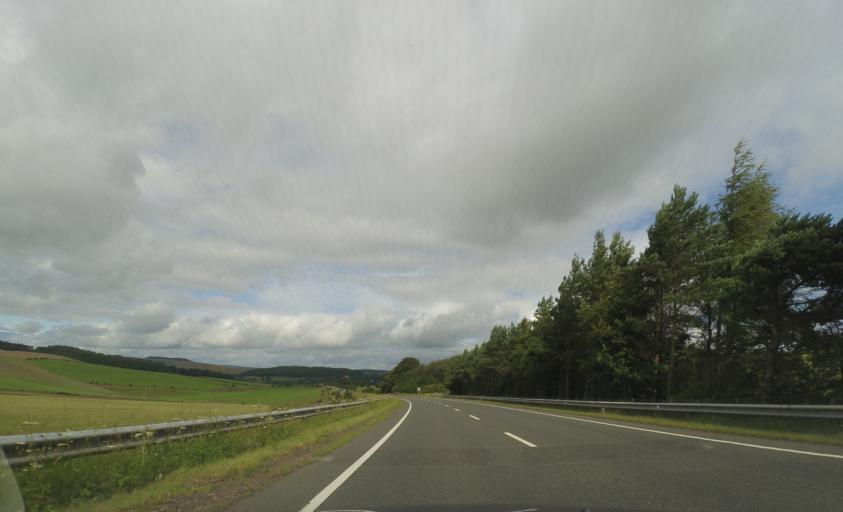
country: GB
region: Scotland
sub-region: The Scottish Borders
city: Hawick
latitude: 55.4800
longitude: -2.8205
